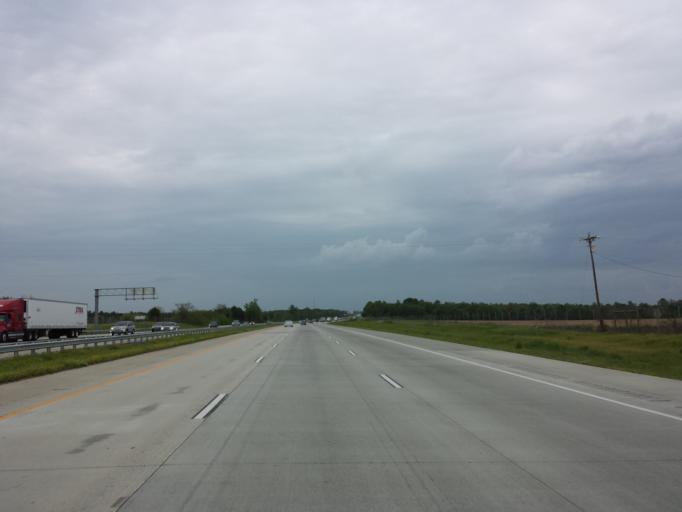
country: US
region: Georgia
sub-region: Dooly County
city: Unadilla
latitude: 32.2118
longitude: -83.7456
